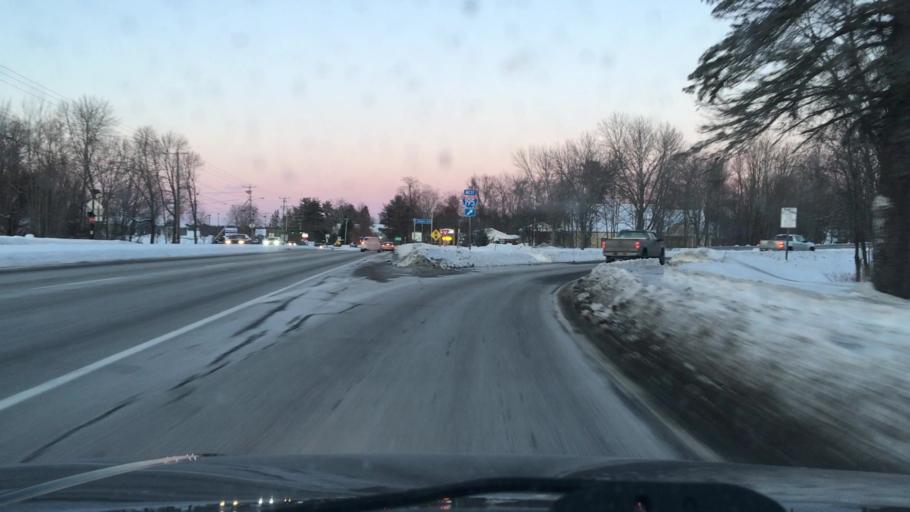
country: US
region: Maine
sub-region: York County
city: Saco
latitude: 43.5124
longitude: -70.4314
